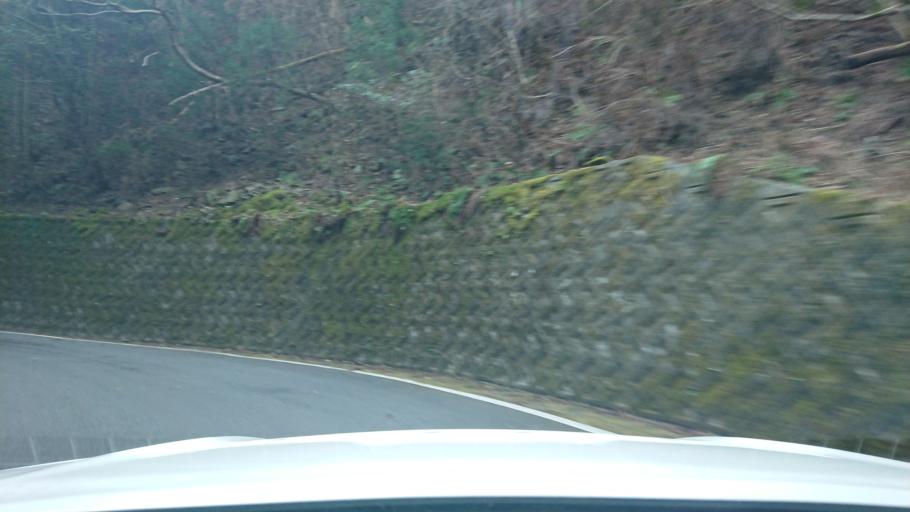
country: JP
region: Tokushima
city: Ishii
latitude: 33.9131
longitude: 134.3989
